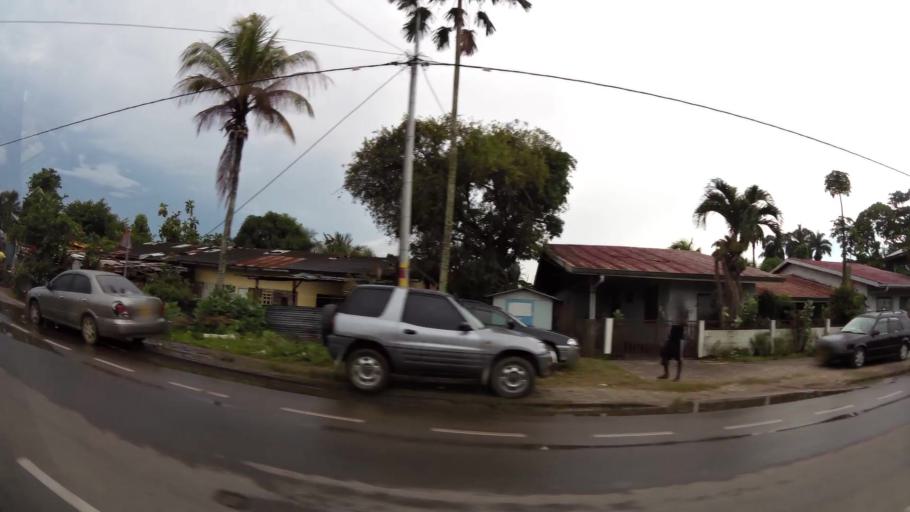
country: SR
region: Paramaribo
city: Paramaribo
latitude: 5.8039
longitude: -55.1825
